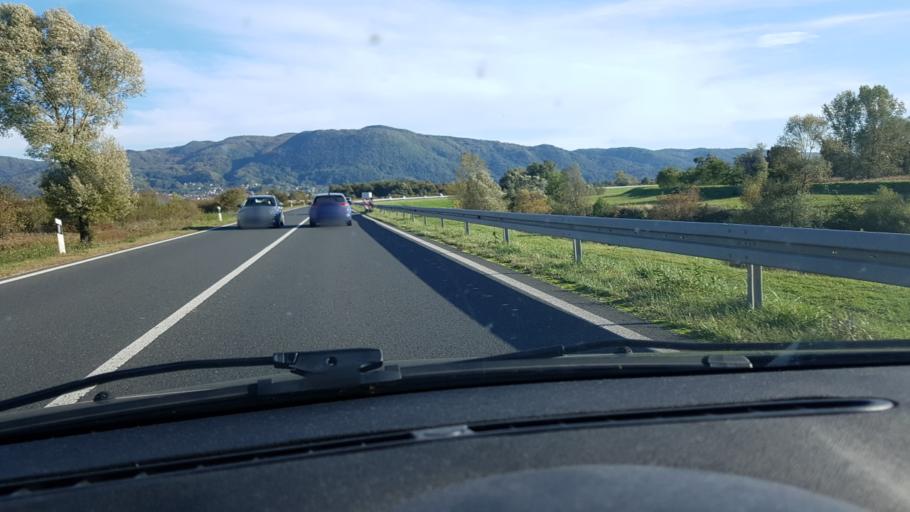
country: HR
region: Zagrebacka
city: Pojatno
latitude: 45.8946
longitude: 15.8183
